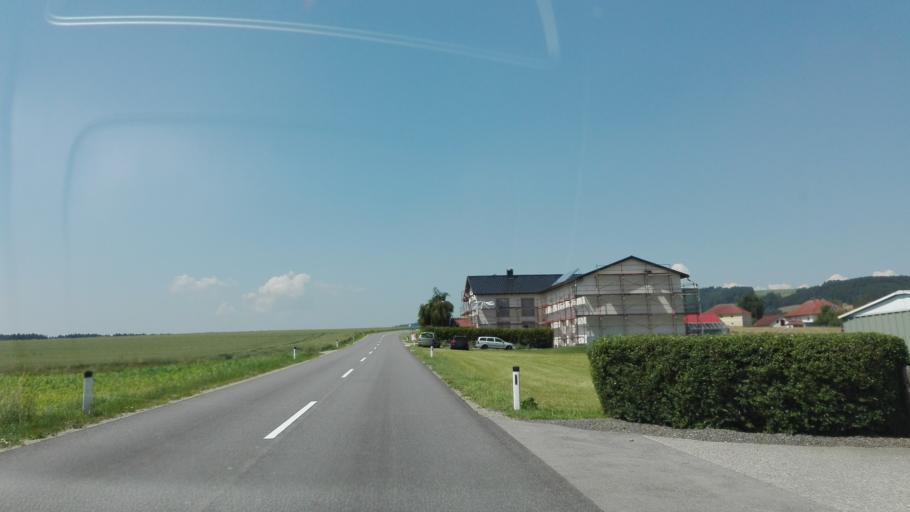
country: AT
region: Upper Austria
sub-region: Politischer Bezirk Grieskirchen
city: Grieskirchen
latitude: 48.3559
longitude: 13.8634
